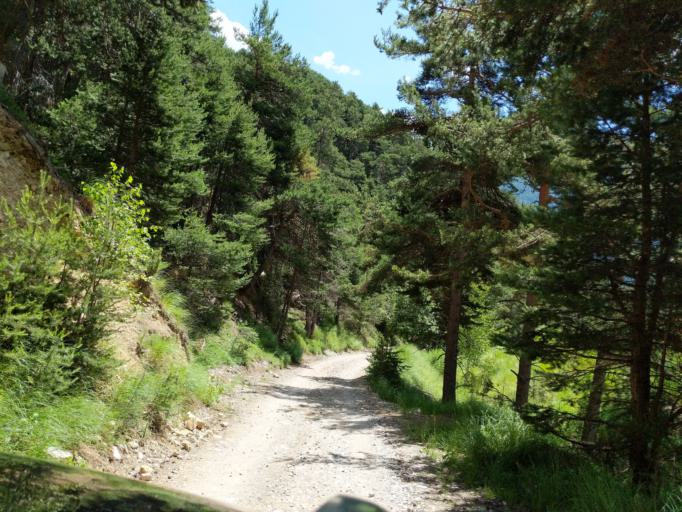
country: FR
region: Rhone-Alpes
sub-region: Departement de la Savoie
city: Modane
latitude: 45.2273
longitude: 6.7476
